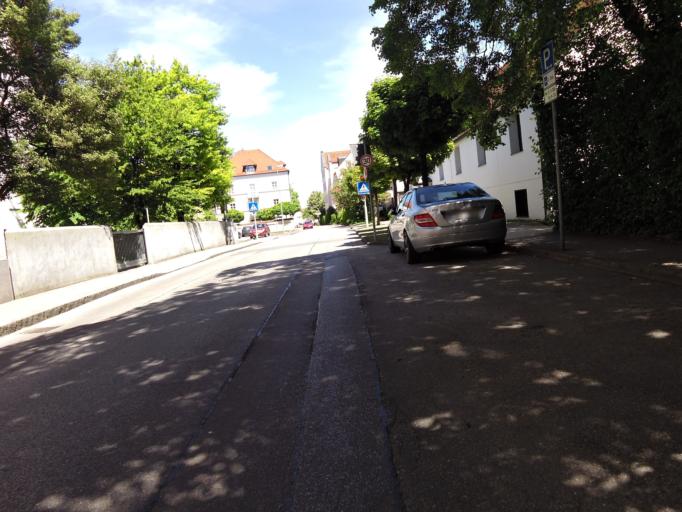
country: DE
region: Bavaria
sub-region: Upper Bavaria
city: Moosburg
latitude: 48.4683
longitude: 11.9379
